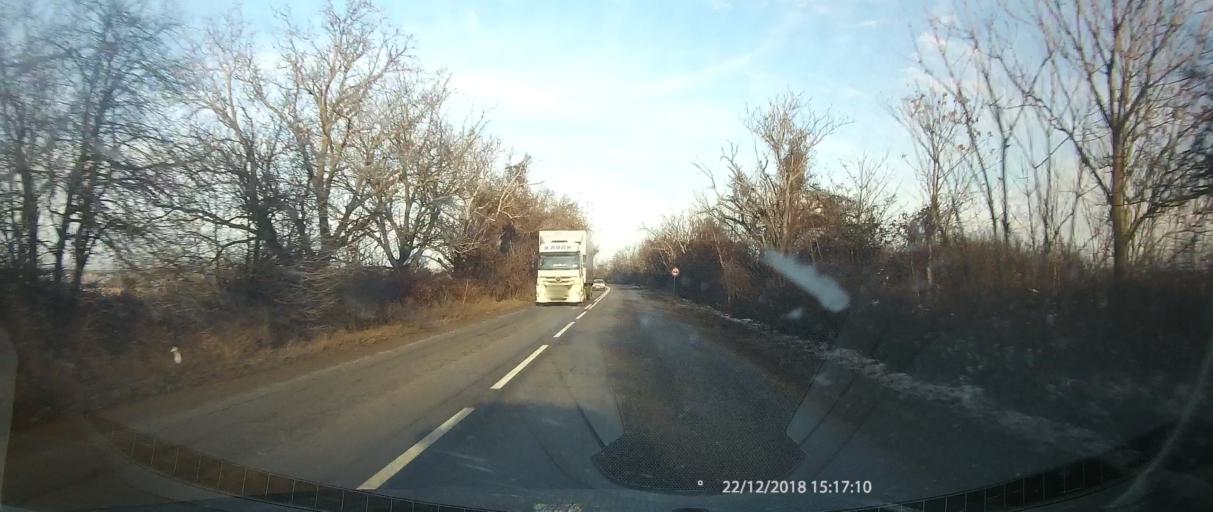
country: BG
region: Ruse
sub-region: Obshtina Dve Mogili
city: Dve Mogili
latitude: 43.6211
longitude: 25.8549
